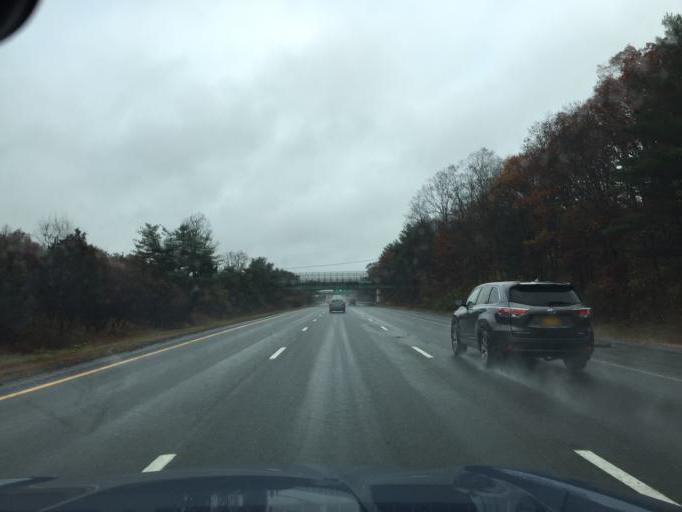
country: US
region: Massachusetts
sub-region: Bristol County
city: Attleboro
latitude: 41.9495
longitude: -71.3078
